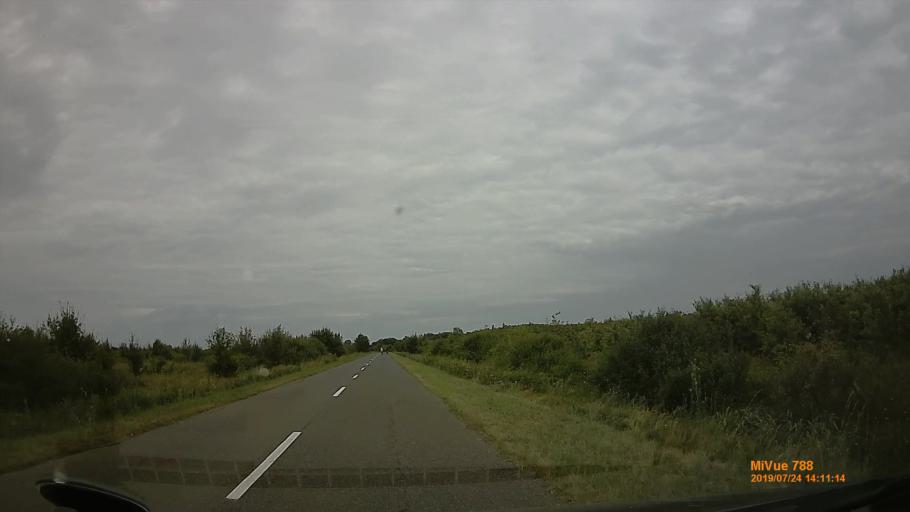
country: HU
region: Szabolcs-Szatmar-Bereg
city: Mandok
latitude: 48.3167
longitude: 22.2958
